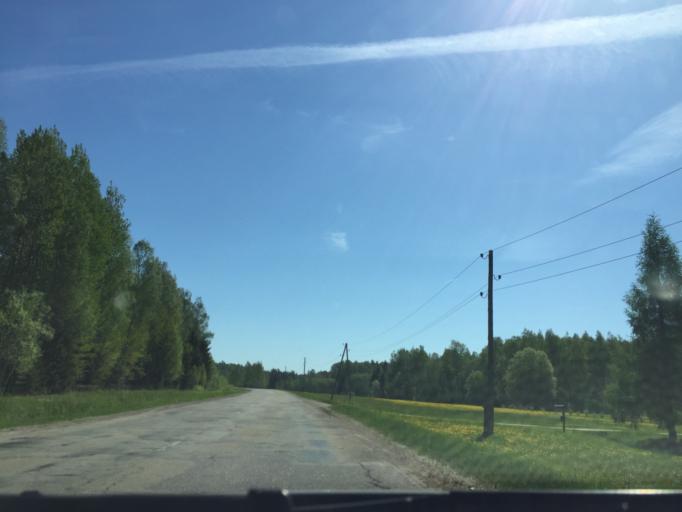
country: LV
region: Incukalns
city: Incukalns
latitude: 57.0231
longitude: 24.7602
